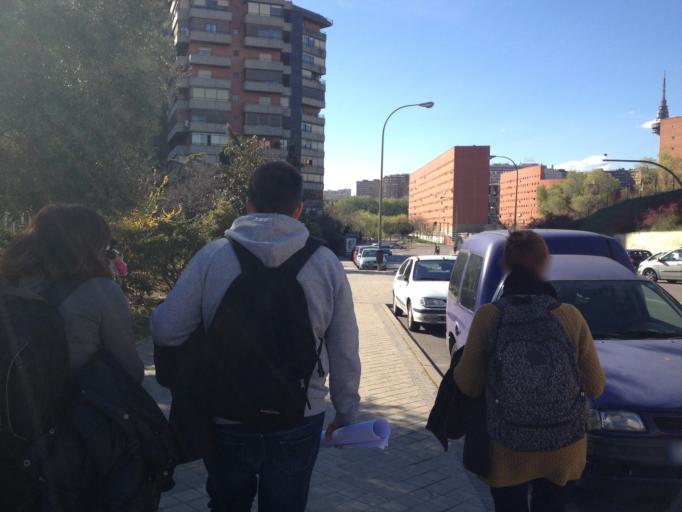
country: ES
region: Madrid
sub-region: Provincia de Madrid
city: Moratalaz
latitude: 40.4130
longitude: -3.6561
